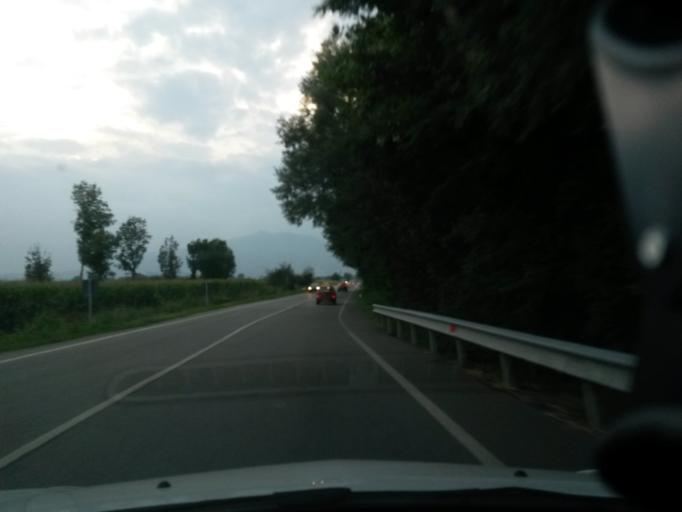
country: IT
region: Piedmont
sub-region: Provincia di Torino
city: Milanere
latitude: 45.0959
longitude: 7.4498
